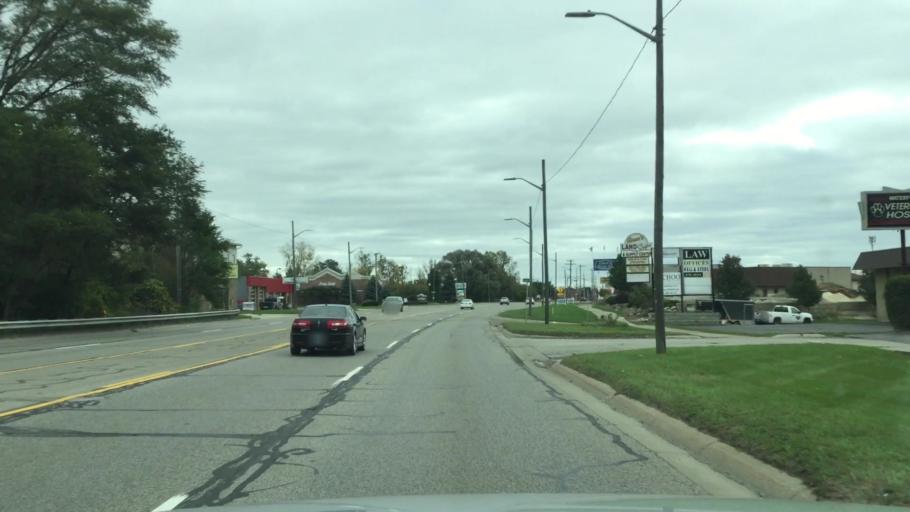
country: US
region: Michigan
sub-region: Oakland County
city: Waterford
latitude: 42.6573
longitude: -83.3783
